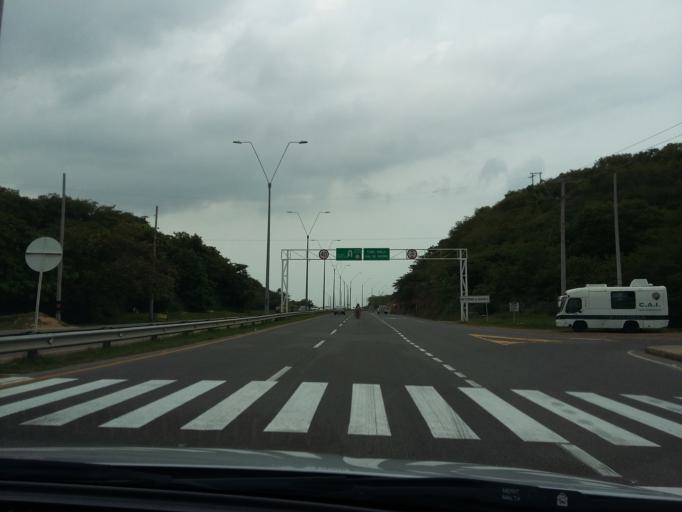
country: CO
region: Bolivar
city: Santa Rosa
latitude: 10.5153
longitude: -75.4693
